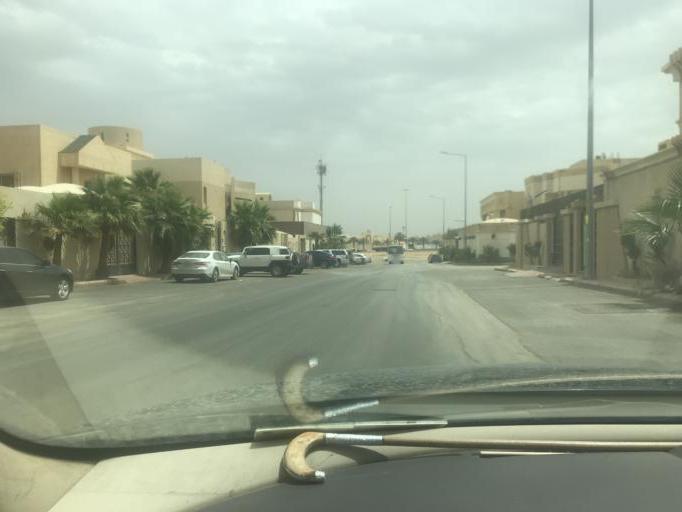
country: SA
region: Ar Riyad
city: Riyadh
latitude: 24.7926
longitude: 46.7153
